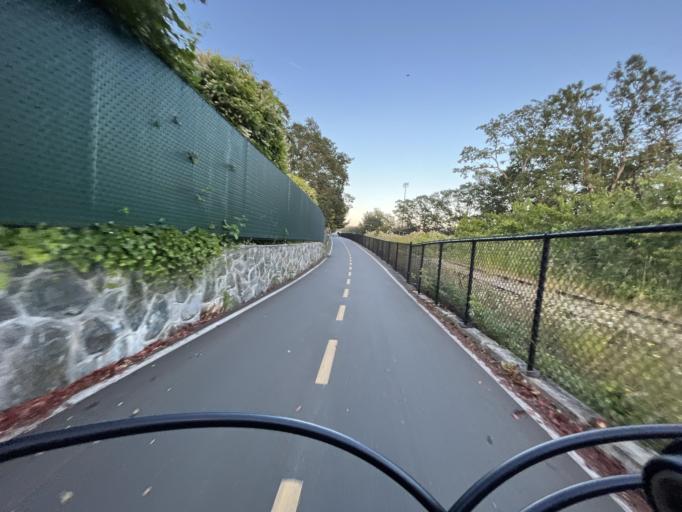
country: CA
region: British Columbia
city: Victoria
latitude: 48.4379
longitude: -123.4267
